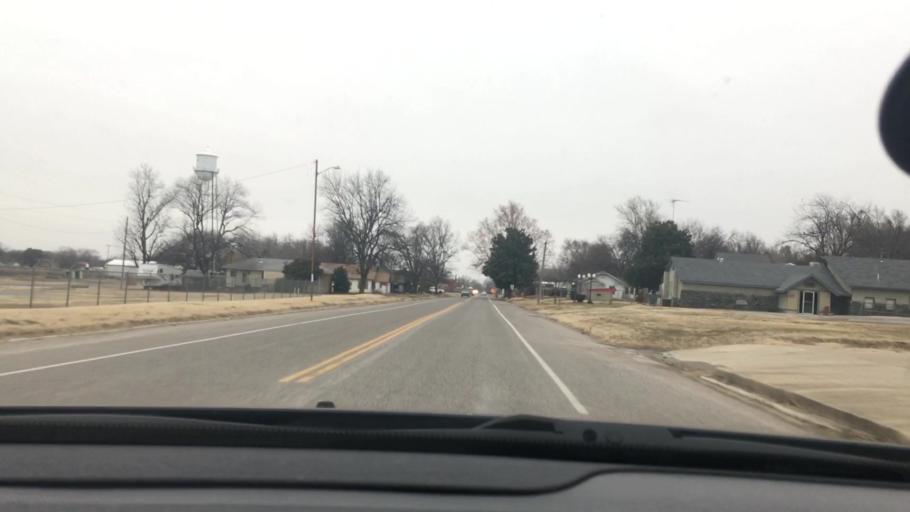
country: US
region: Oklahoma
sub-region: Garvin County
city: Wynnewood
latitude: 34.6368
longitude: -97.1692
